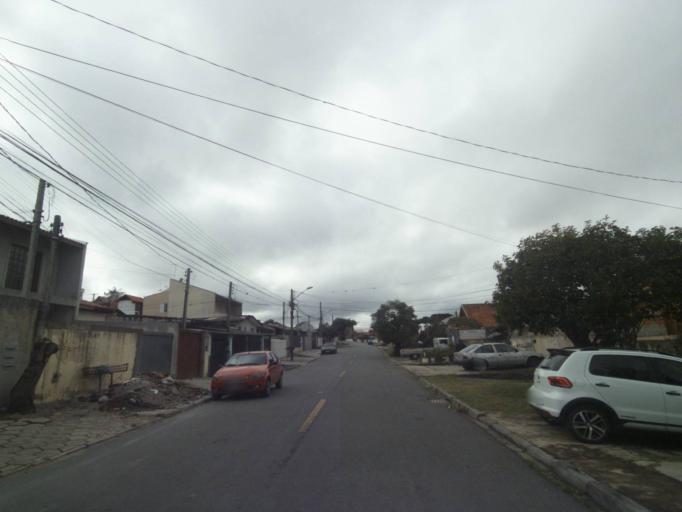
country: BR
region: Parana
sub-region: Curitiba
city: Curitiba
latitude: -25.5028
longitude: -49.2883
